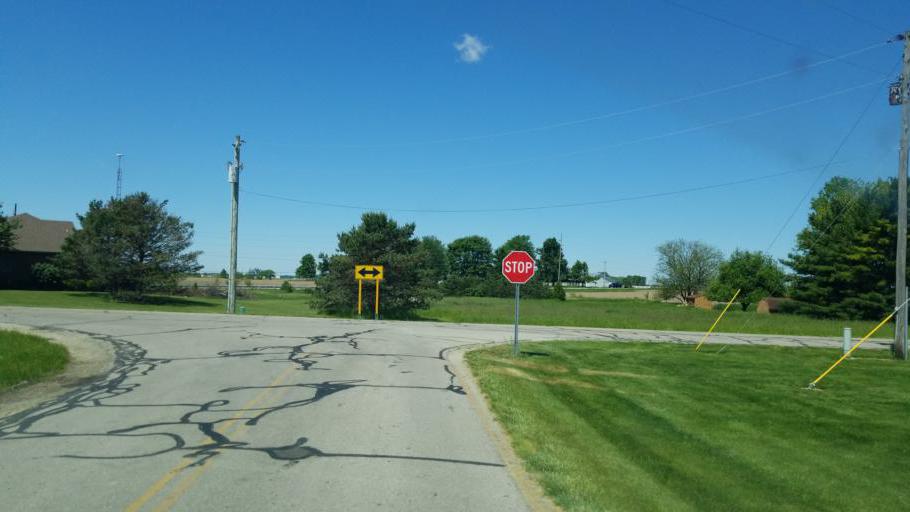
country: US
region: Ohio
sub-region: Shelby County
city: Anna
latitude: 40.3802
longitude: -84.2400
